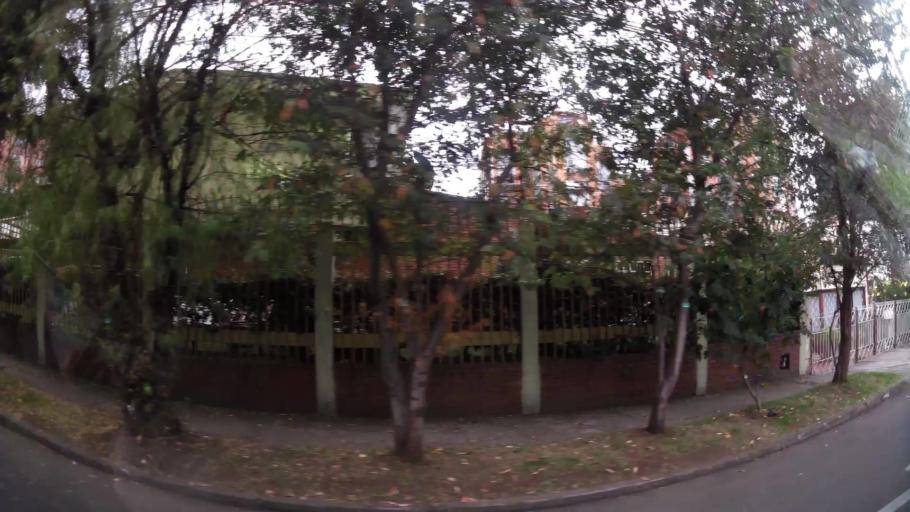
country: CO
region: Bogota D.C.
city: Barrio San Luis
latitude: 4.6884
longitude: -74.0701
